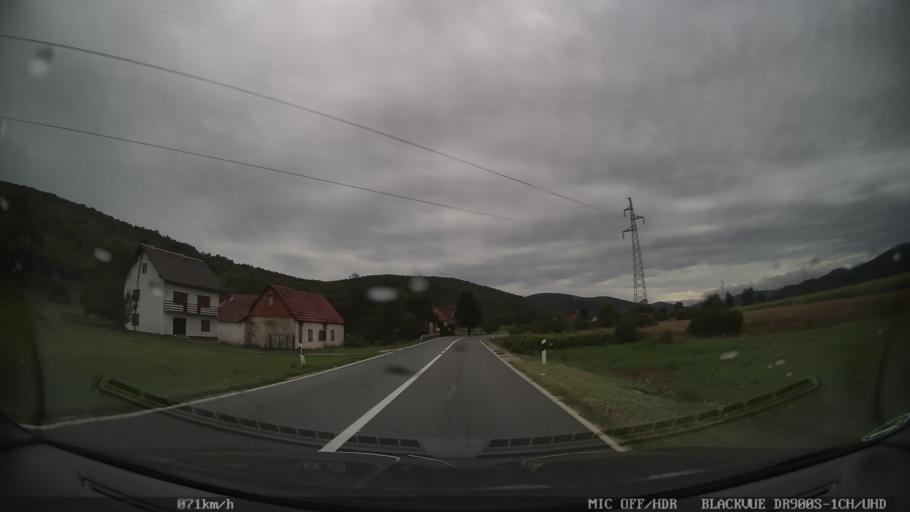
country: HR
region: Licko-Senjska
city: Brinje
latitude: 44.9191
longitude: 15.1505
